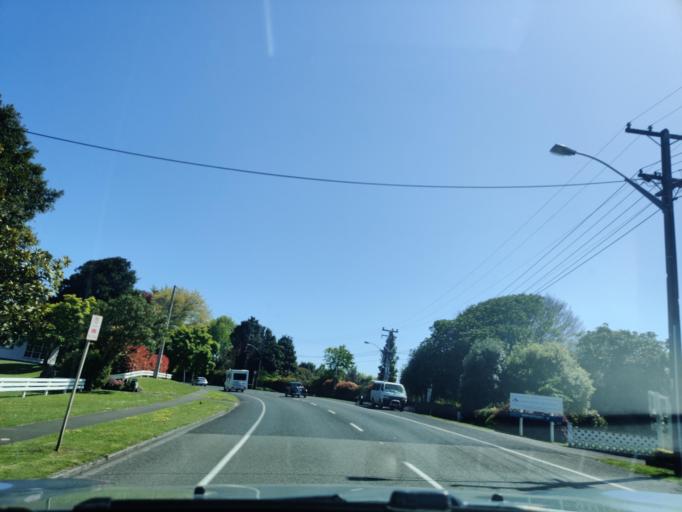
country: NZ
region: Manawatu-Wanganui
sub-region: Wanganui District
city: Wanganui
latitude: -39.9111
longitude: 175.0263
